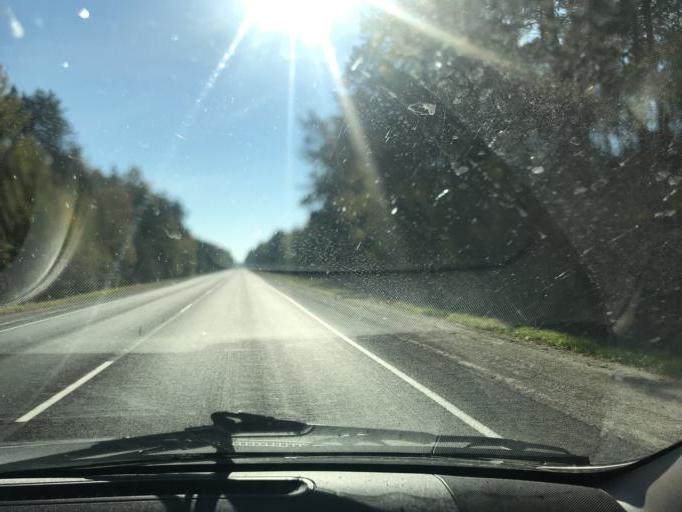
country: BY
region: Brest
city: Mikashevichy
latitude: 52.2662
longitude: 27.4410
